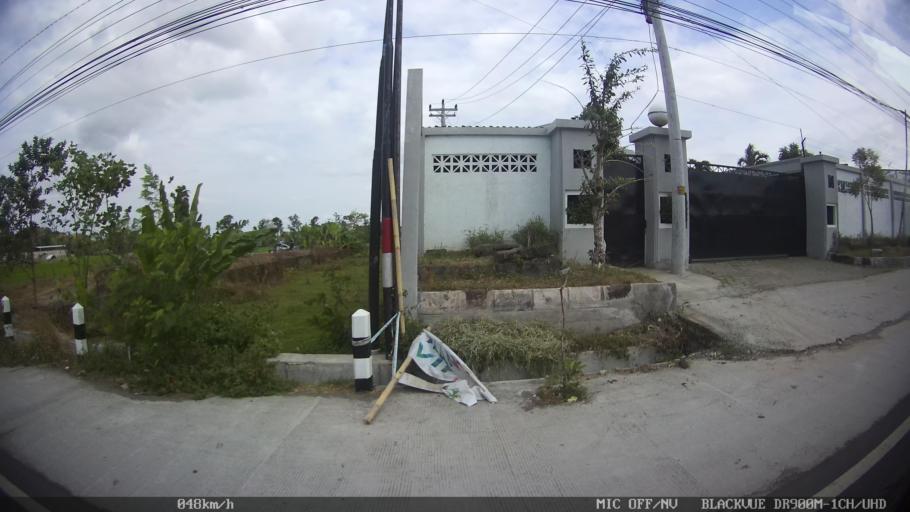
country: ID
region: Central Java
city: Candi Prambanan
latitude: -7.7985
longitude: 110.4828
